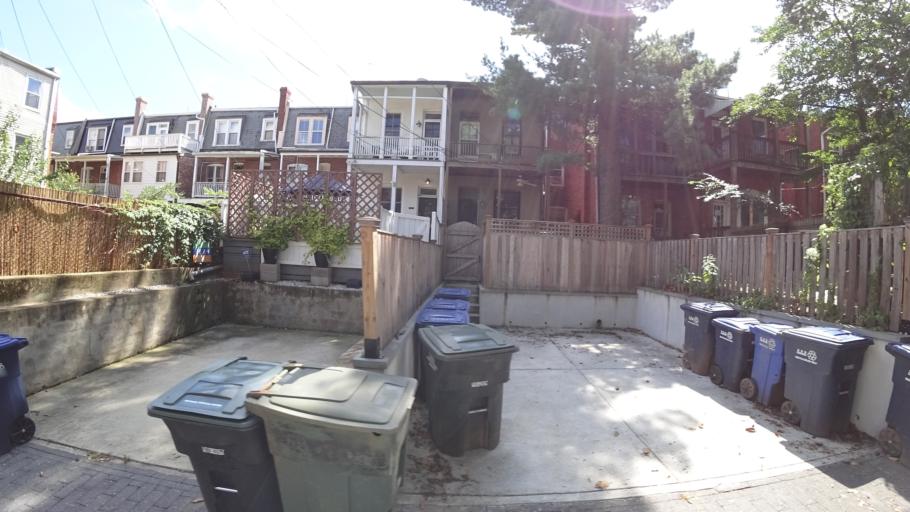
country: US
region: Washington, D.C.
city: Washington, D.C.
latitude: 38.9337
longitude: -77.0419
